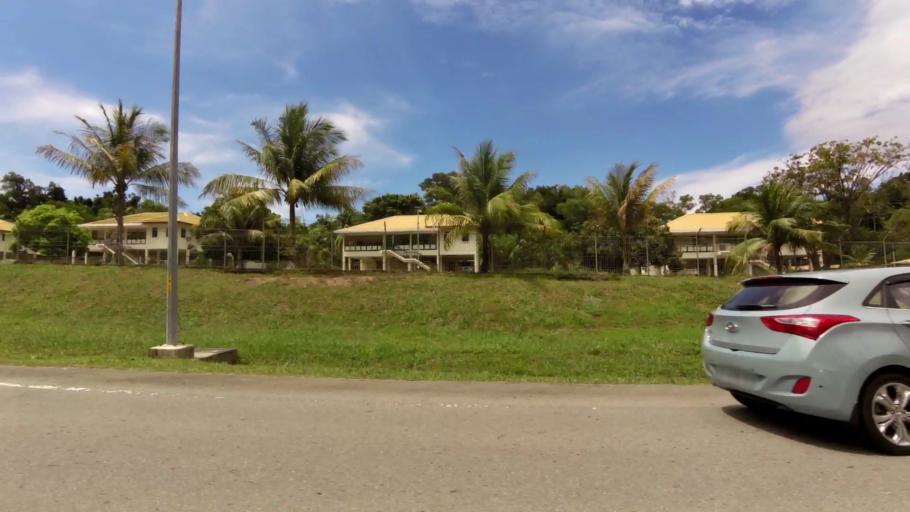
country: BN
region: Brunei and Muara
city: Bandar Seri Begawan
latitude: 4.9950
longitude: 114.9453
